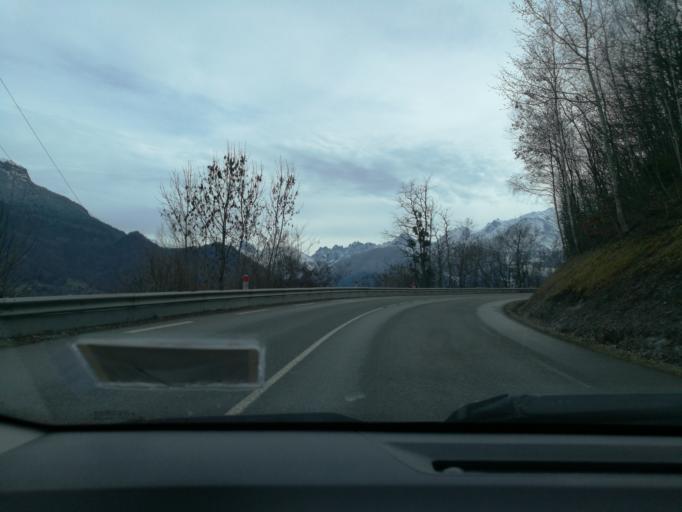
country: FR
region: Rhone-Alpes
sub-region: Departement de la Haute-Savoie
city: Sallanches
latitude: 45.9281
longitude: 6.6321
